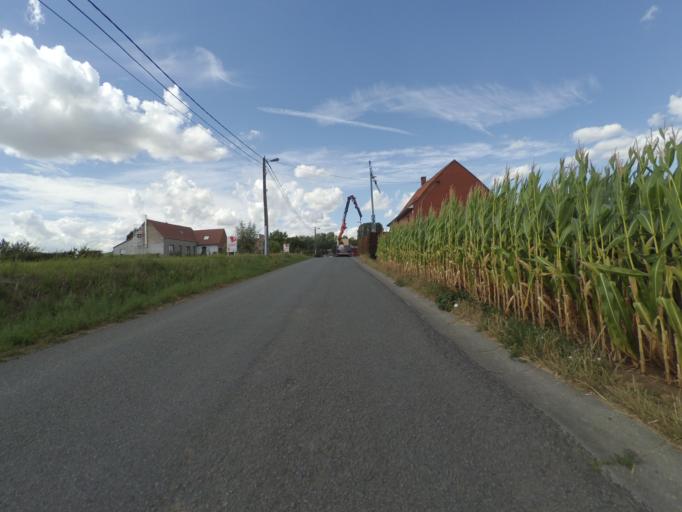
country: BE
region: Wallonia
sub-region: Province du Hainaut
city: Frasnes-lez-Buissenal
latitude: 50.6742
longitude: 3.6130
